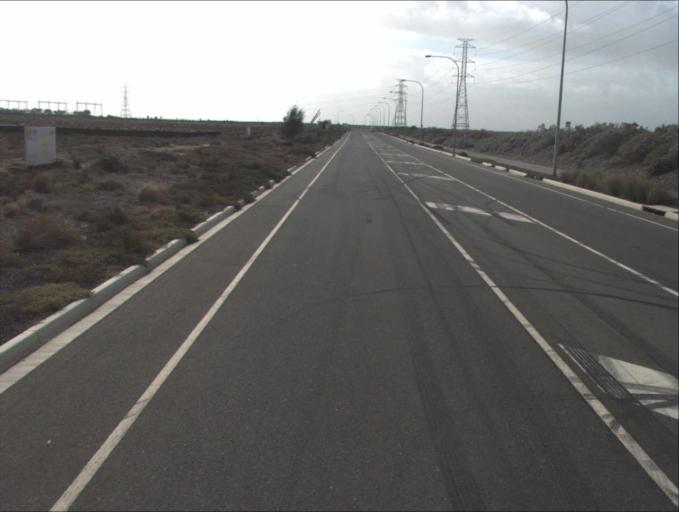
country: AU
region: South Australia
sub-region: Port Adelaide Enfield
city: Birkenhead
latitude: -34.7756
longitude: 138.5087
